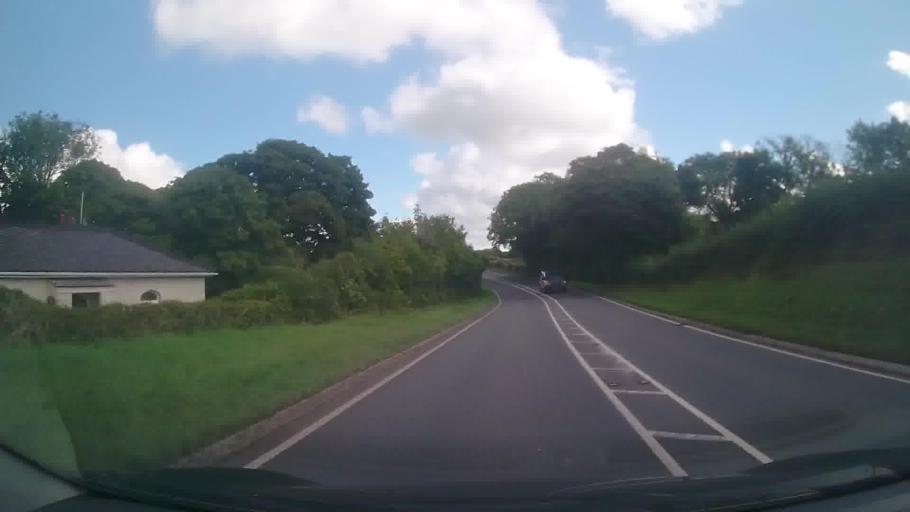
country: GB
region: Wales
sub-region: Pembrokeshire
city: Pembroke
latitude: 51.6808
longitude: -4.8890
